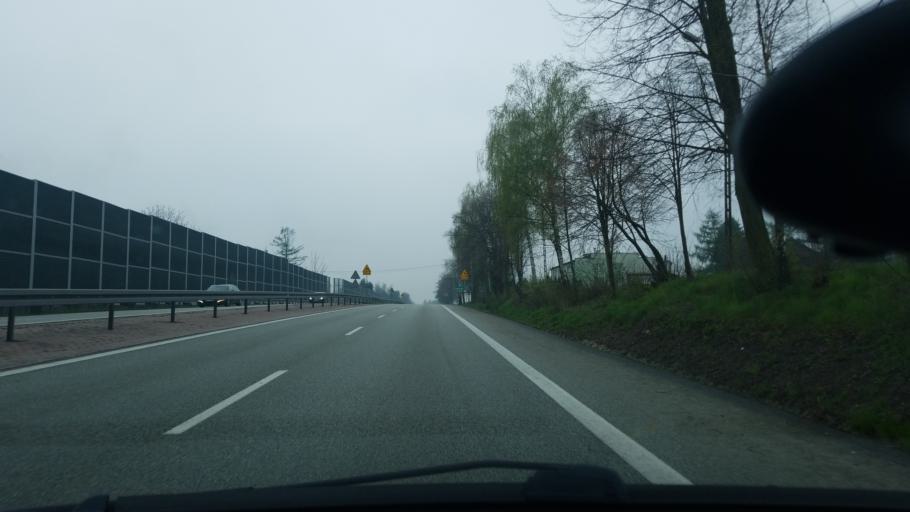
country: PL
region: Silesian Voivodeship
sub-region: Powiat pszczynski
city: Pawlowice
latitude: 49.9907
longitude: 18.7118
